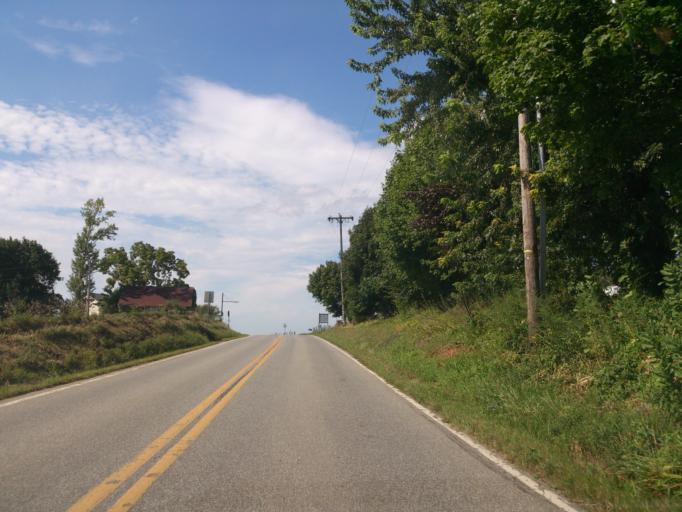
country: US
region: Pennsylvania
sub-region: York County
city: Susquehanna Trails
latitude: 39.7782
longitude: -76.4657
